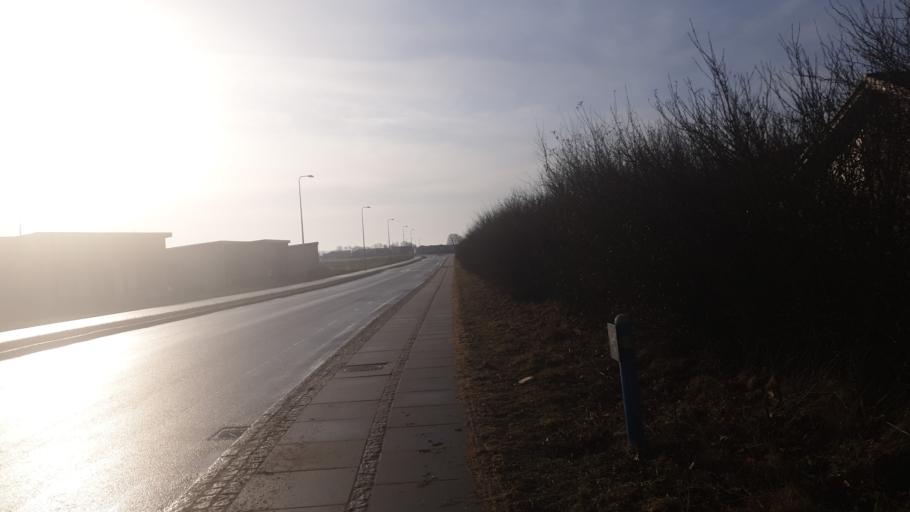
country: DK
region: Central Jutland
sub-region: Hedensted Kommune
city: Hedensted
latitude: 55.7655
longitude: 9.7228
